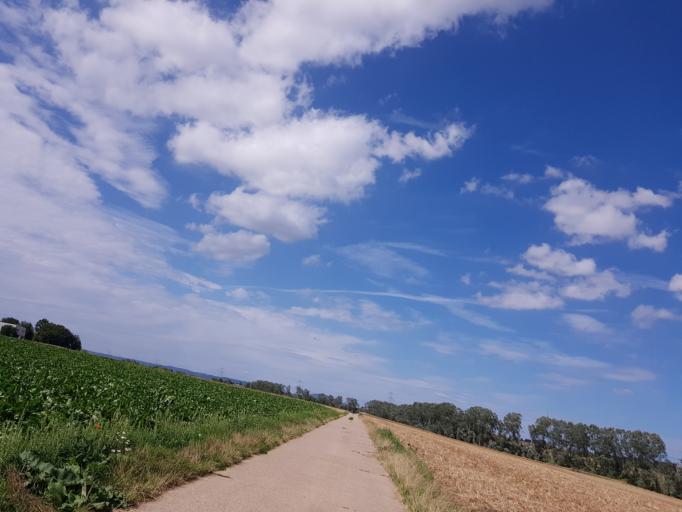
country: DE
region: Hesse
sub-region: Regierungsbezirk Giessen
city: Langgons
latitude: 50.5087
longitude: 8.6614
